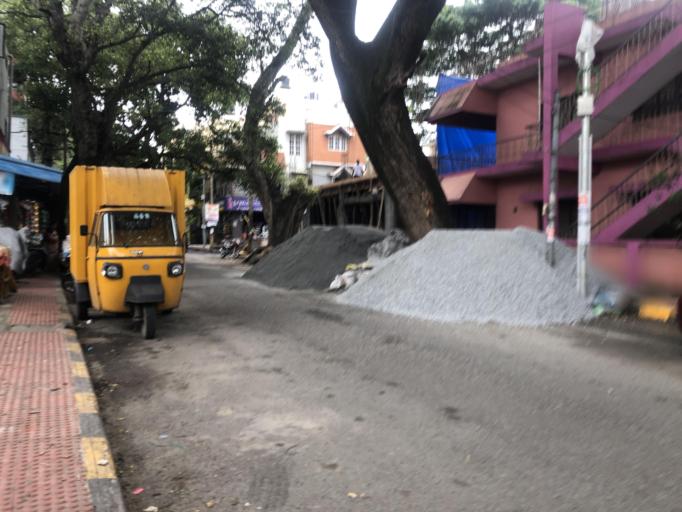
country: IN
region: Karnataka
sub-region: Bangalore Urban
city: Bangalore
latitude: 12.9397
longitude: 77.5423
